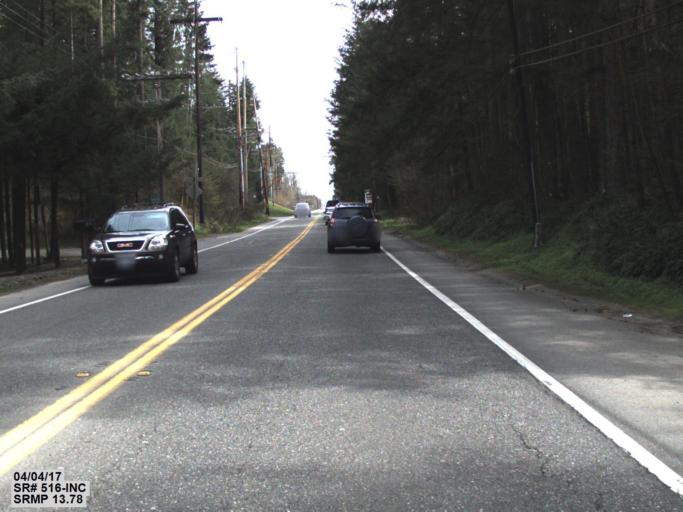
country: US
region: Washington
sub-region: King County
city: Lake Morton-Berrydale
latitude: 47.3581
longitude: -122.0717
